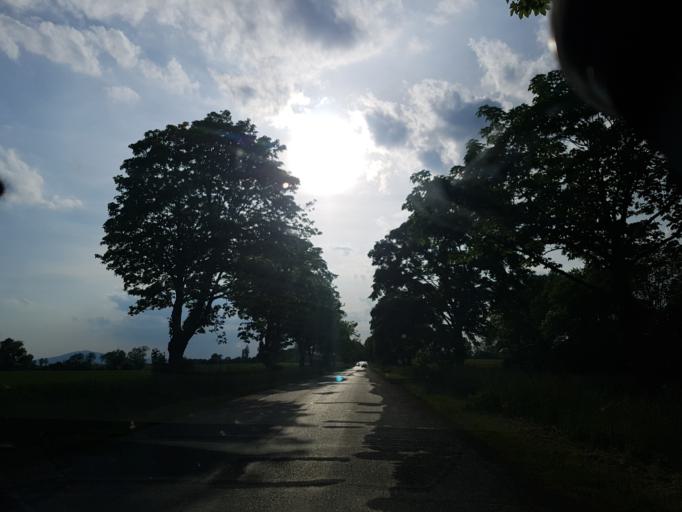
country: PL
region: Lower Silesian Voivodeship
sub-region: Powiat wroclawski
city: Kobierzyce
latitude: 50.9164
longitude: 16.9744
